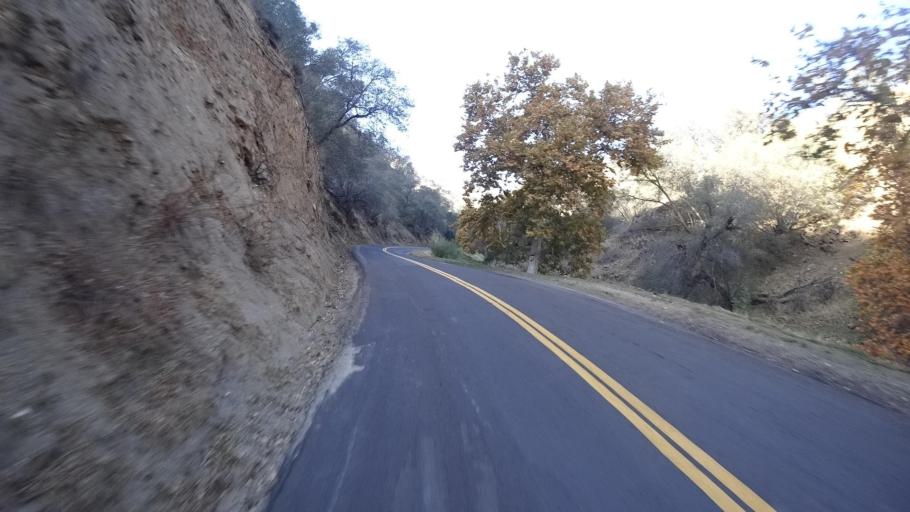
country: US
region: California
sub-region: Kern County
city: Bear Valley Springs
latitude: 35.3211
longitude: -118.5904
